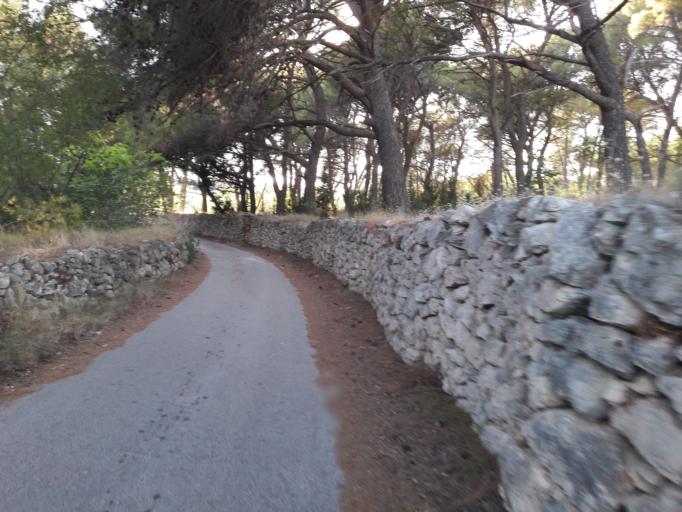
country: HR
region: Sibensko-Kniniska
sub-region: Grad Sibenik
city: Sibenik
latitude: 43.6950
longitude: 15.8430
